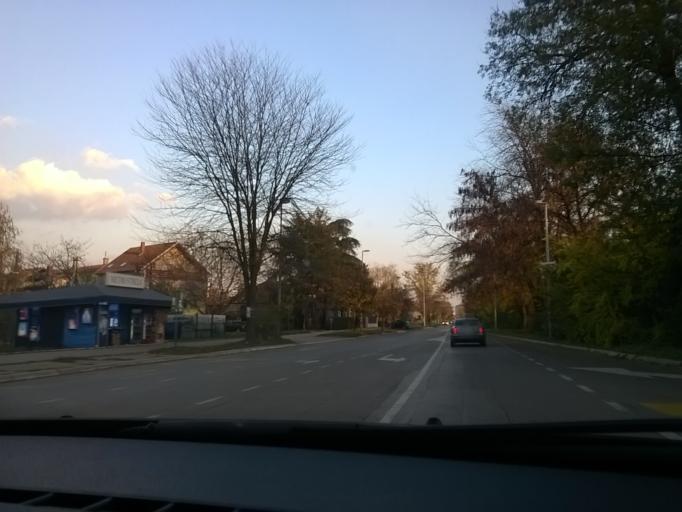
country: RS
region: Autonomna Pokrajina Vojvodina
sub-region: Juznobanatski Okrug
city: Pancevo
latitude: 44.8645
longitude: 20.6598
